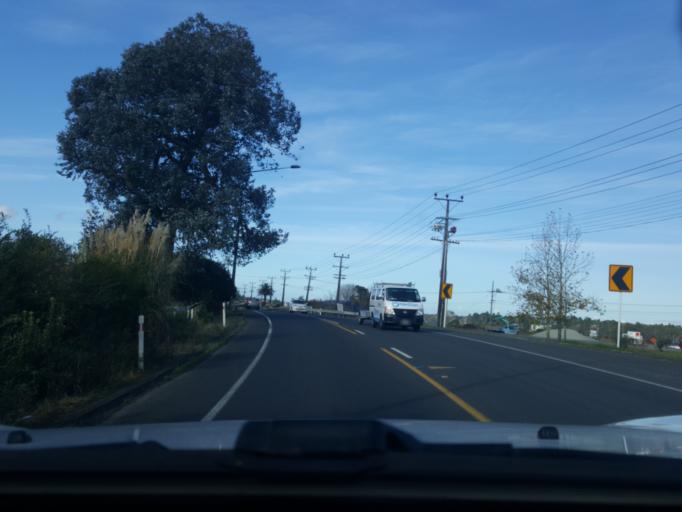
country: NZ
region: Auckland
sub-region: Auckland
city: Muriwai Beach
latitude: -36.7715
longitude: 174.5365
